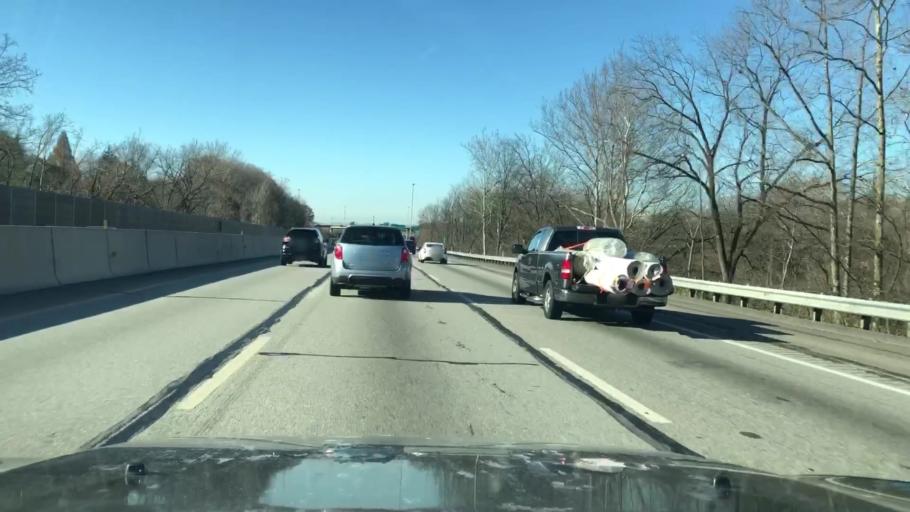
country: US
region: Pennsylvania
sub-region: Montgomery County
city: Plymouth Meeting
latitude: 40.1148
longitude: -75.2677
